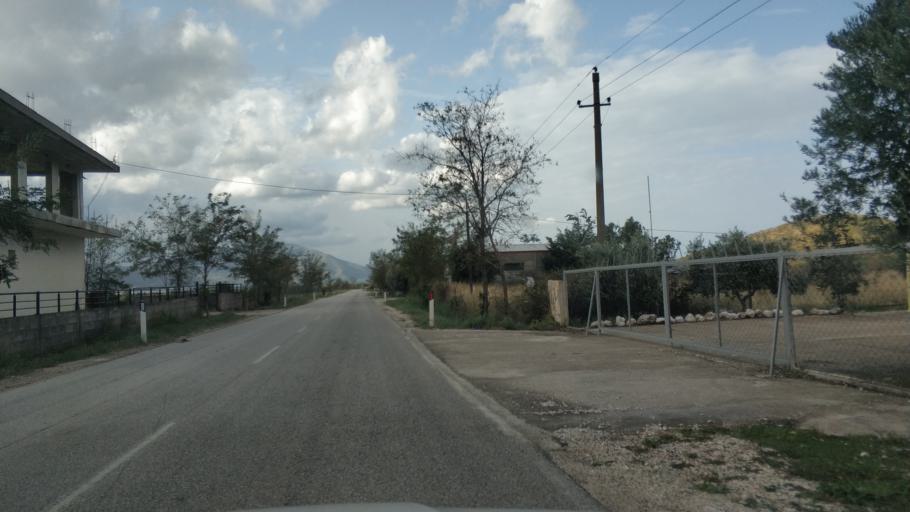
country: AL
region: Vlore
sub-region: Rrethi i Vlores
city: Orikum
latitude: 40.2849
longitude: 19.4975
